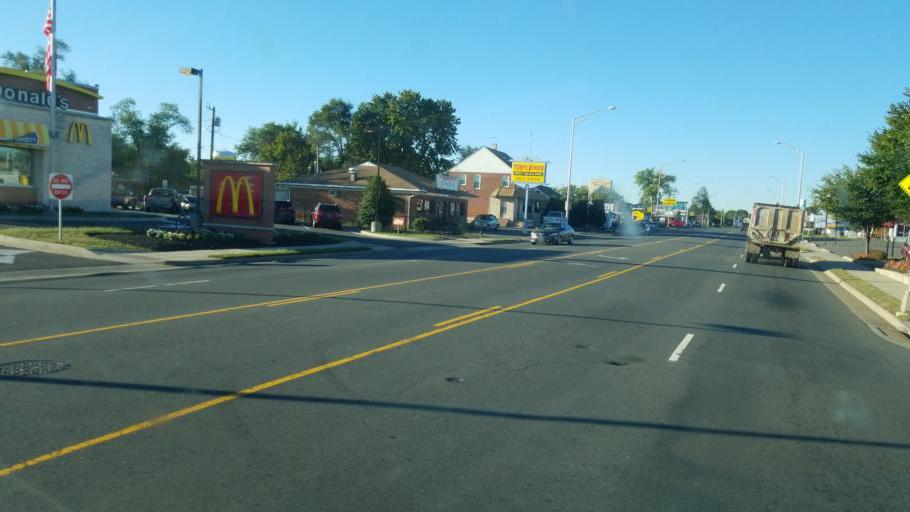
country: US
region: Virginia
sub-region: City of Manassas
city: Manassas
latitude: 38.7603
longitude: -77.4618
